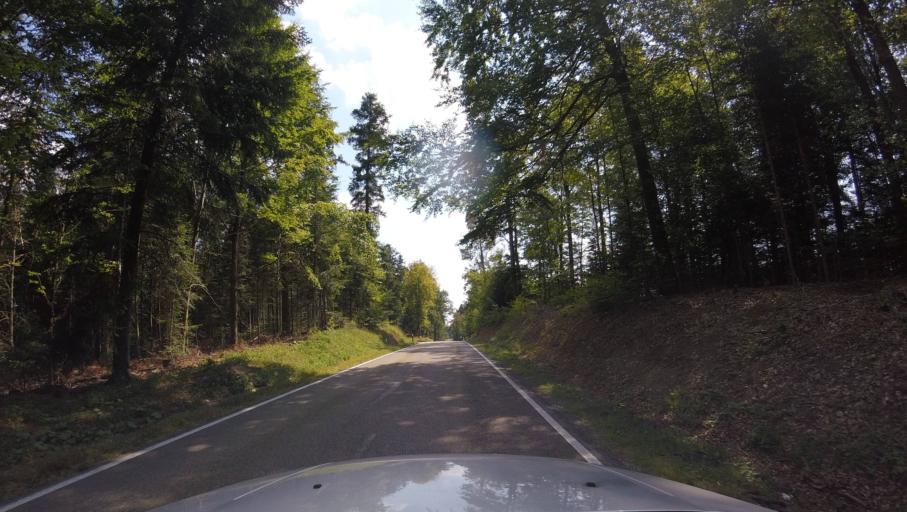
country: DE
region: Baden-Wuerttemberg
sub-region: Regierungsbezirk Stuttgart
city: Kaisersbach
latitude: 48.9365
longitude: 9.6096
